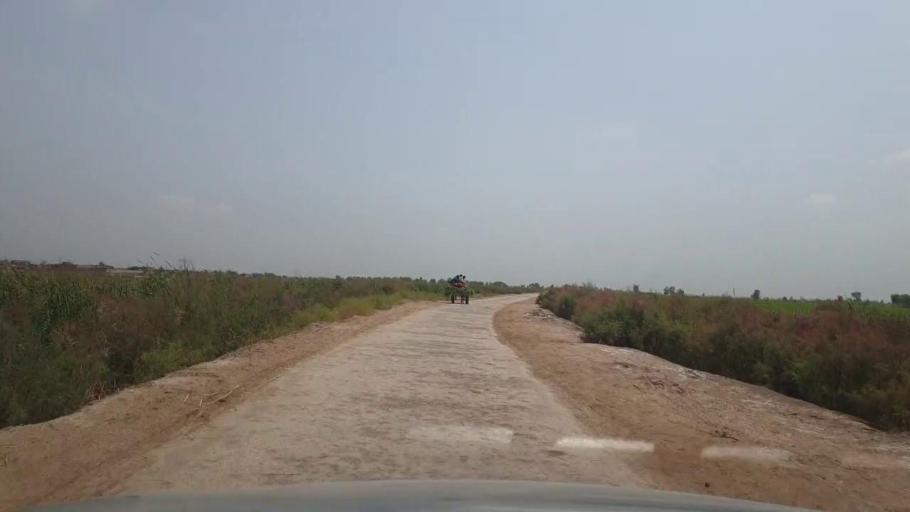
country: PK
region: Sindh
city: Garhi Yasin
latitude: 27.9416
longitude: 68.3840
